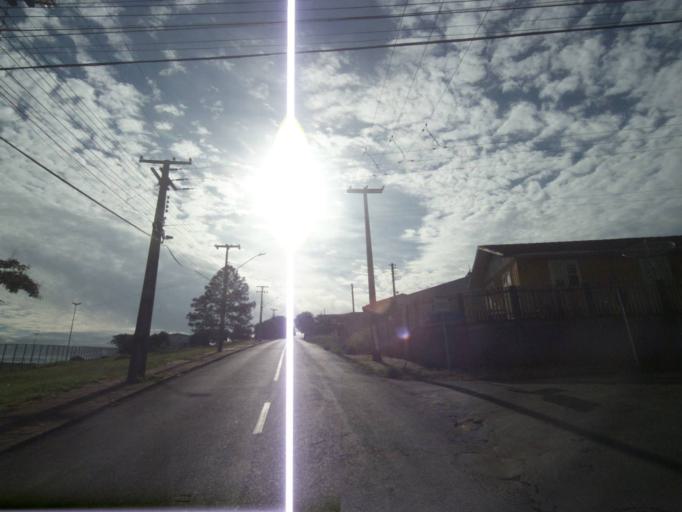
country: BR
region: Parana
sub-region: Telemaco Borba
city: Telemaco Borba
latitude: -24.3448
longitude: -50.6084
